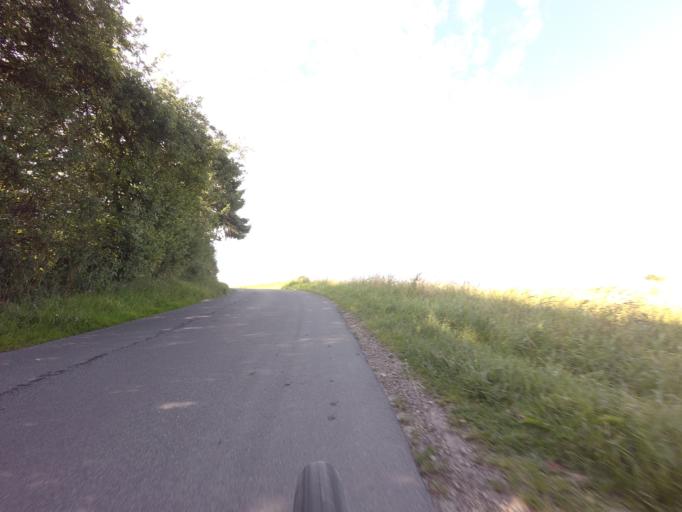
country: DK
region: Central Jutland
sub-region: Skanderborg Kommune
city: Stilling
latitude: 56.0644
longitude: 9.9665
